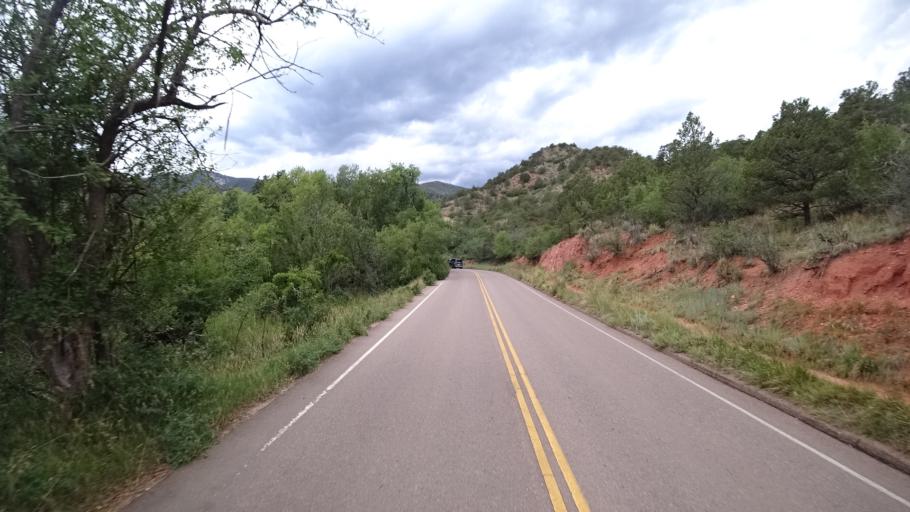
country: US
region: Colorado
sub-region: El Paso County
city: Manitou Springs
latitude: 38.8446
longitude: -104.9012
